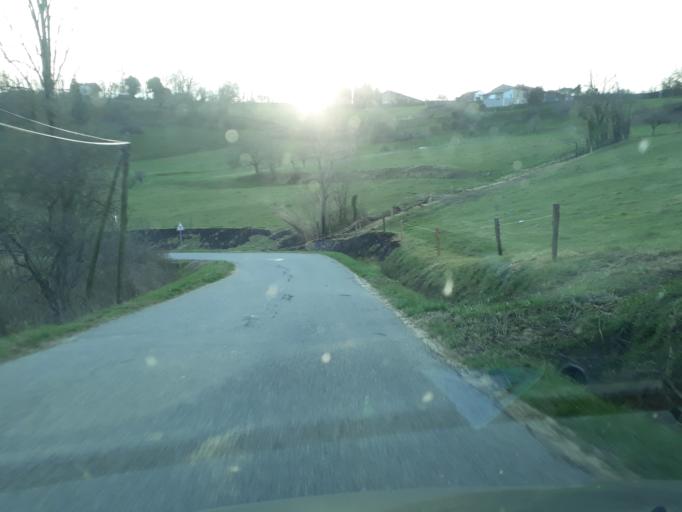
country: FR
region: Midi-Pyrenees
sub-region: Departement de la Haute-Garonne
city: Montesquieu-Volvestre
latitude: 43.1686
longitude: 1.3160
